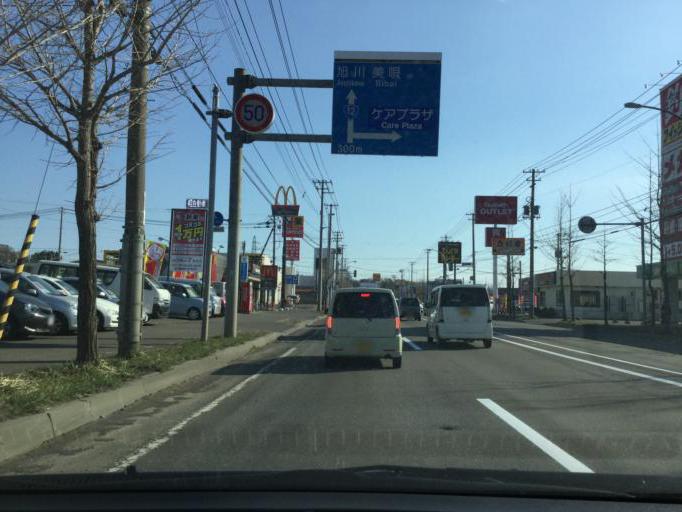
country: JP
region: Hokkaido
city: Iwamizawa
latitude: 43.2029
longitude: 141.7808
